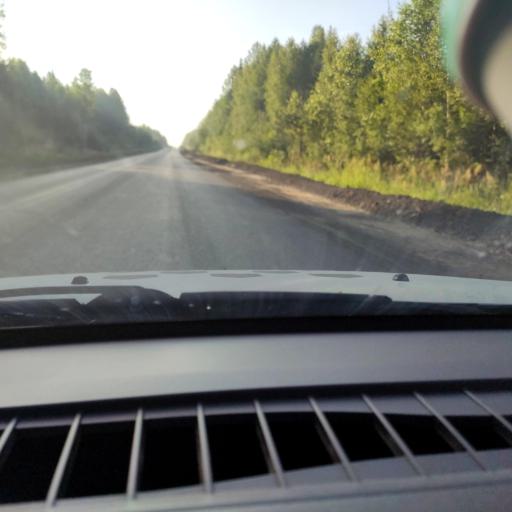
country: RU
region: Kirov
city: Chernaya Kholunitsa
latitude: 58.8707
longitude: 51.5372
